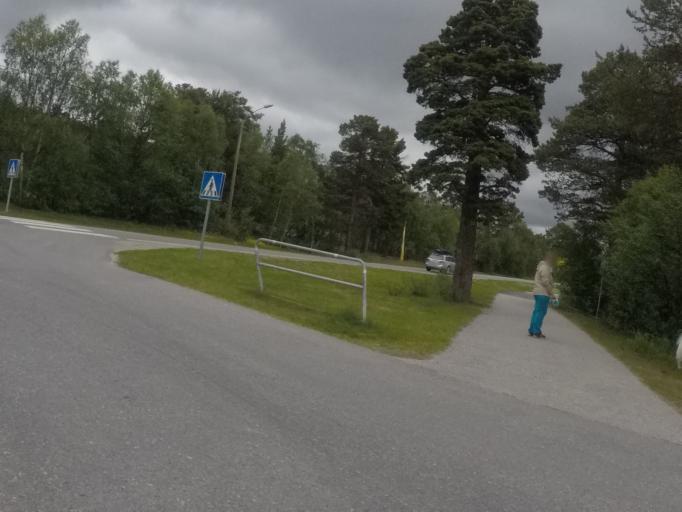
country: NO
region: Finnmark Fylke
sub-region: Karasjok
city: Karasjohka
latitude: 69.4742
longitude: 25.5096
